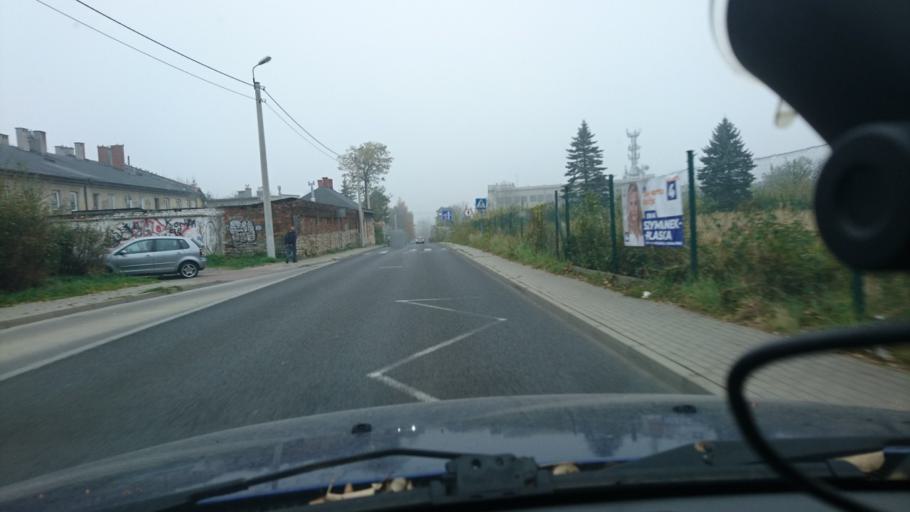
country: PL
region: Silesian Voivodeship
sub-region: Bielsko-Biala
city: Bielsko-Biala
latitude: 49.8193
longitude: 19.0314
